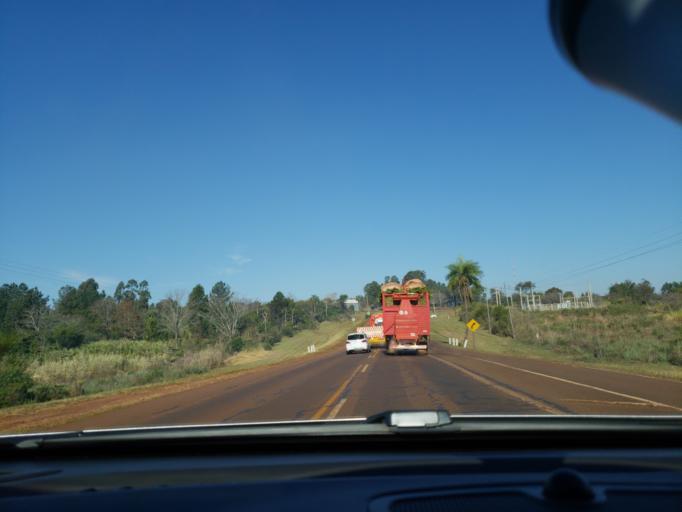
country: AR
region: Misiones
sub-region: Departamento de Apostoles
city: San Jose
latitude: -27.7596
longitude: -55.7732
